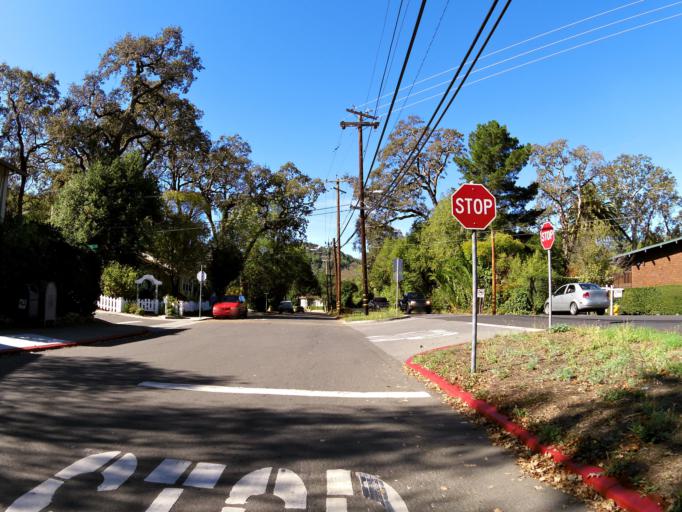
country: US
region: California
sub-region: Marin County
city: San Anselmo
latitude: 37.9775
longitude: -122.5674
